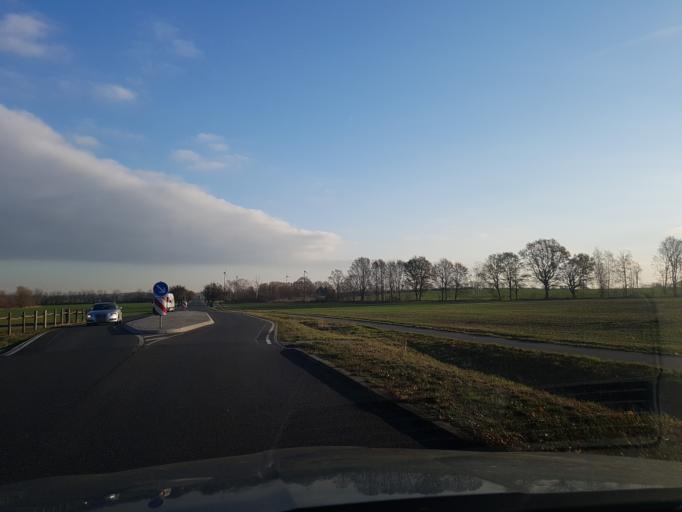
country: DE
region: Brandenburg
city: Luckau
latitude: 51.8342
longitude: 13.6469
